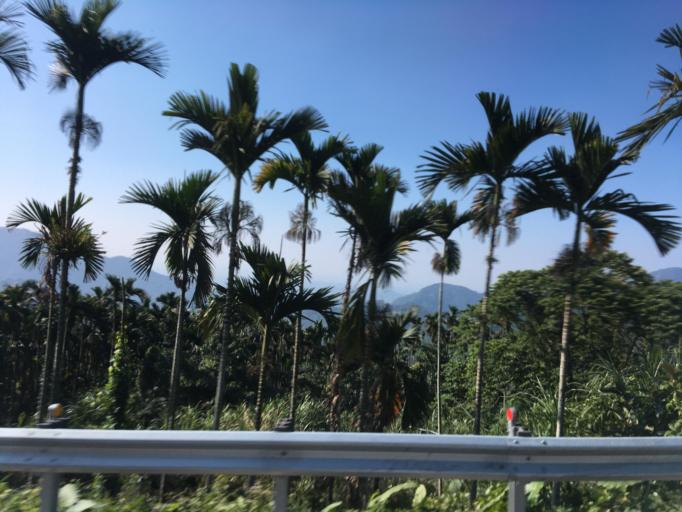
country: TW
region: Taiwan
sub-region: Chiayi
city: Jiayi Shi
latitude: 23.4290
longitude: 120.6413
